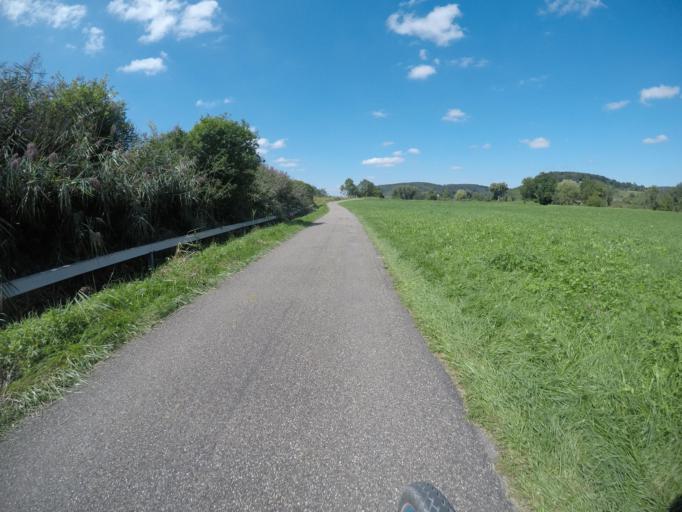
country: DE
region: Baden-Wuerttemberg
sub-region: Tuebingen Region
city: Tuebingen
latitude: 48.5193
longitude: 9.0246
